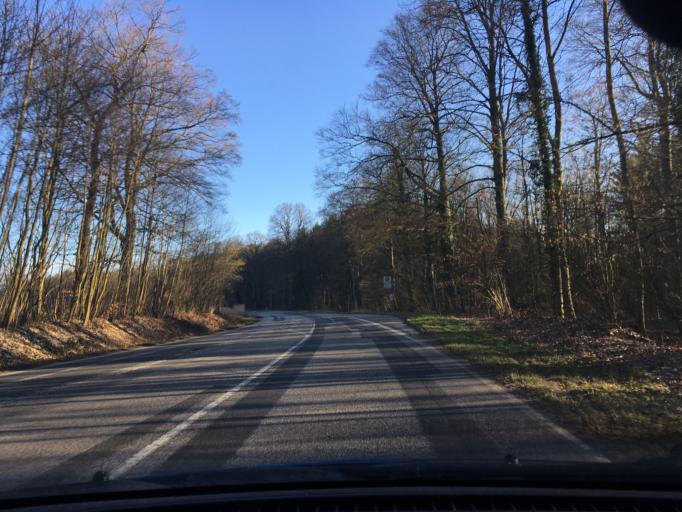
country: DE
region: Schleswig-Holstein
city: Schnakenbek
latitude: 53.3765
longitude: 10.5164
